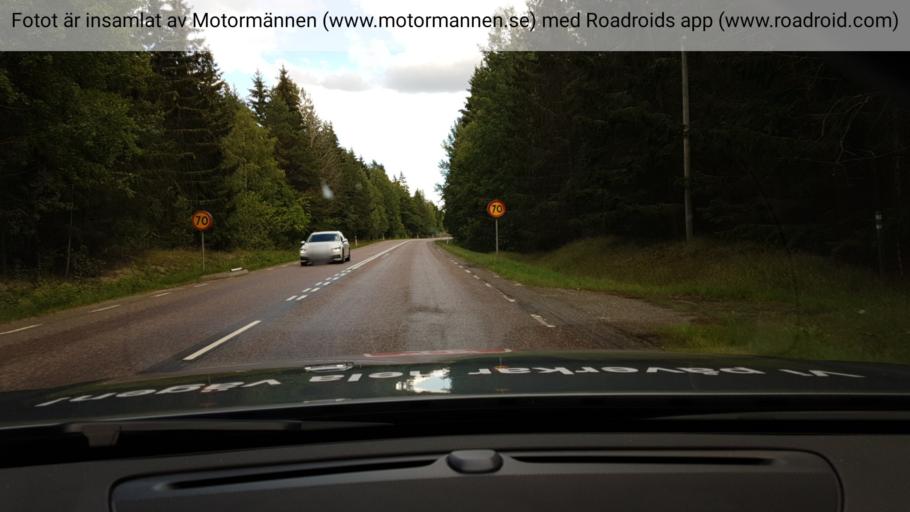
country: SE
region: Soedermanland
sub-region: Strangnas Kommun
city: Akers Styckebruk
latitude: 59.2951
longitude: 17.1040
